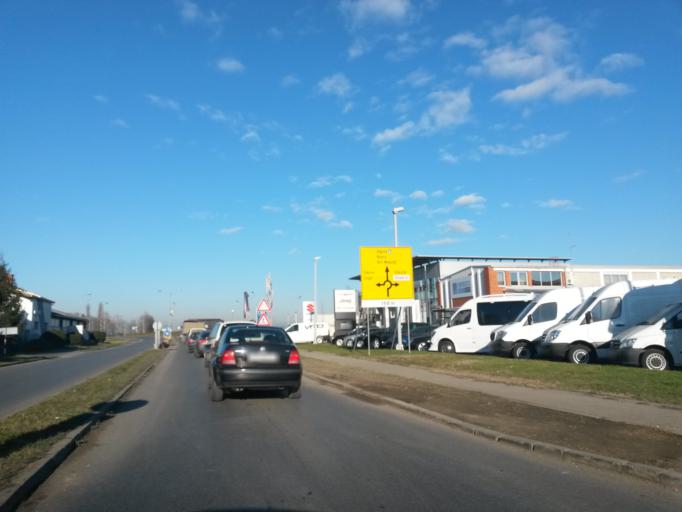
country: HR
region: Osjecko-Baranjska
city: Brijest
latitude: 45.5400
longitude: 18.6489
